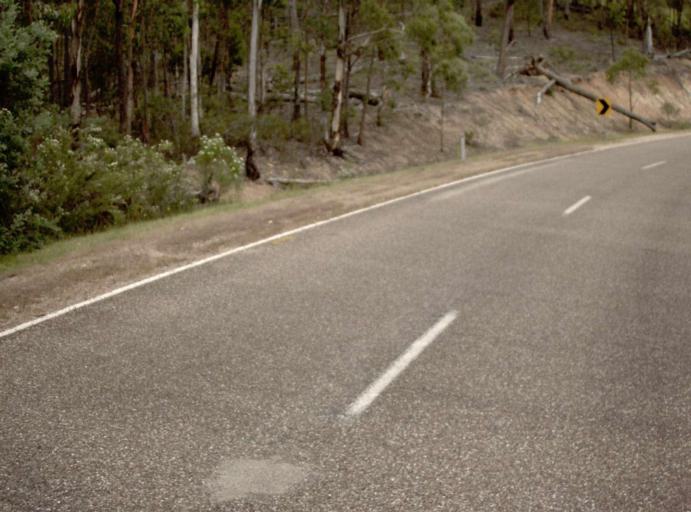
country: AU
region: Victoria
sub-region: East Gippsland
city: Bairnsdale
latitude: -37.6526
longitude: 147.2783
